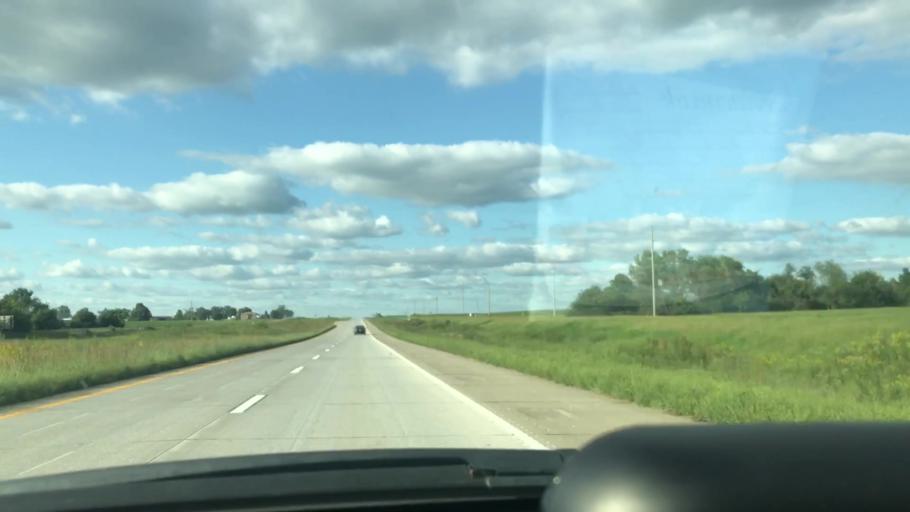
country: US
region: Missouri
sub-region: Benton County
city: Cole Camp
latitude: 38.4947
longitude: -93.2735
